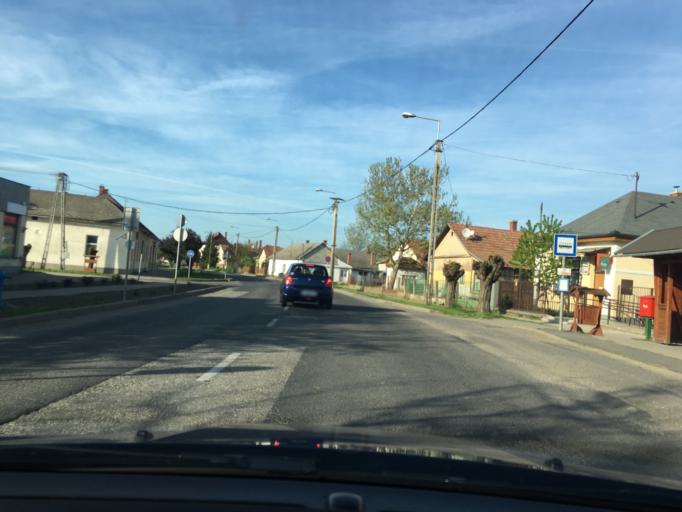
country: HU
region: Hajdu-Bihar
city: Csokmo
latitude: 47.0287
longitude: 21.2947
